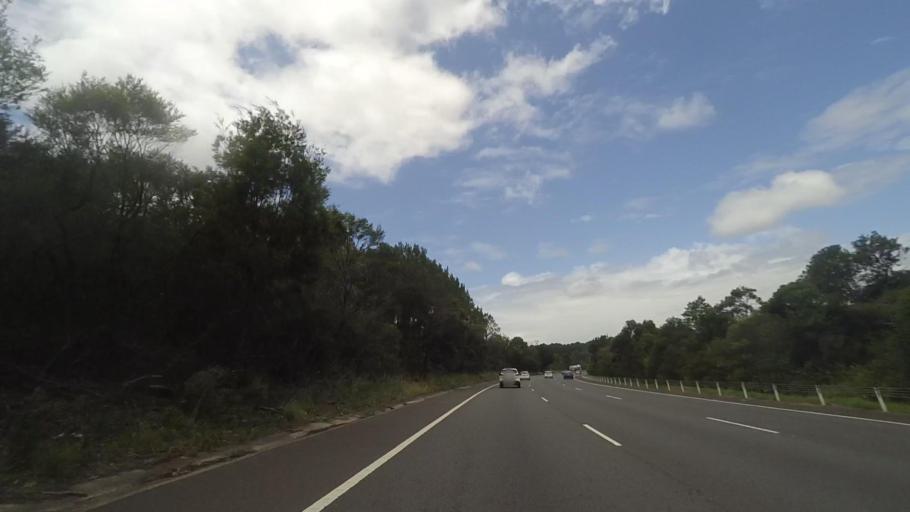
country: AU
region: New South Wales
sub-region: Gosford Shire
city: Narara
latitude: -33.3674
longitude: 151.3112
